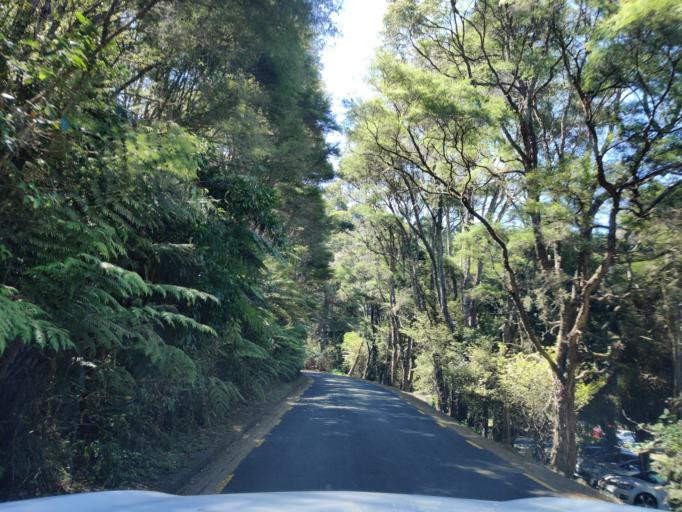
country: NZ
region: Auckland
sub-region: Auckland
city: Red Hill
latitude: -37.0666
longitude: 175.0890
